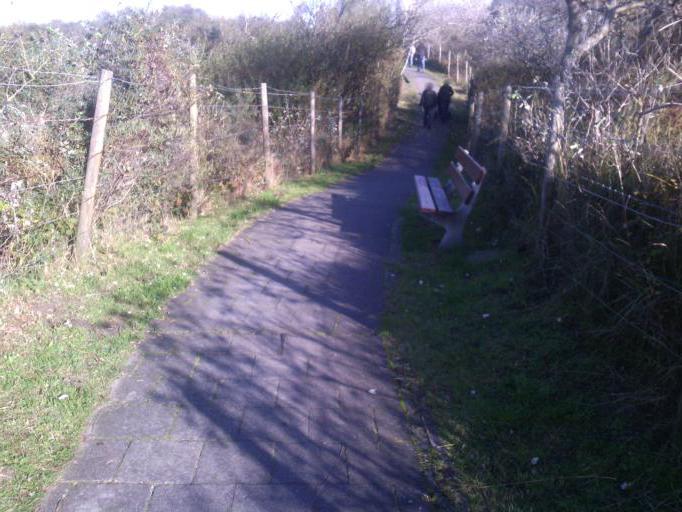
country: BE
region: Flanders
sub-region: Provincie West-Vlaanderen
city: Middelkerke
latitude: 51.1743
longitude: 2.7865
